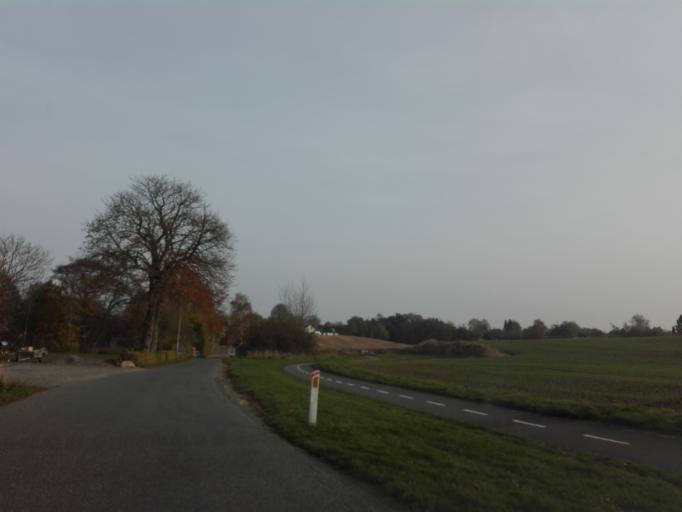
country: DK
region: Central Jutland
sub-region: Arhus Kommune
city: Marslet
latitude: 56.0682
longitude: 10.1514
